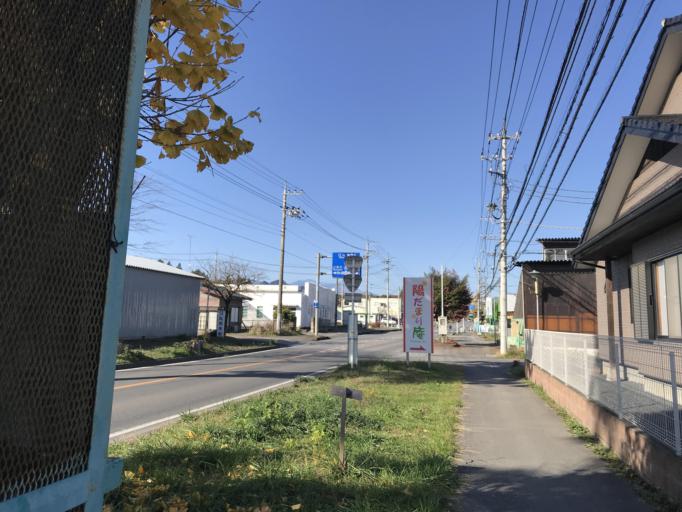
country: JP
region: Tochigi
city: Kanuma
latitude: 36.5861
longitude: 139.7493
